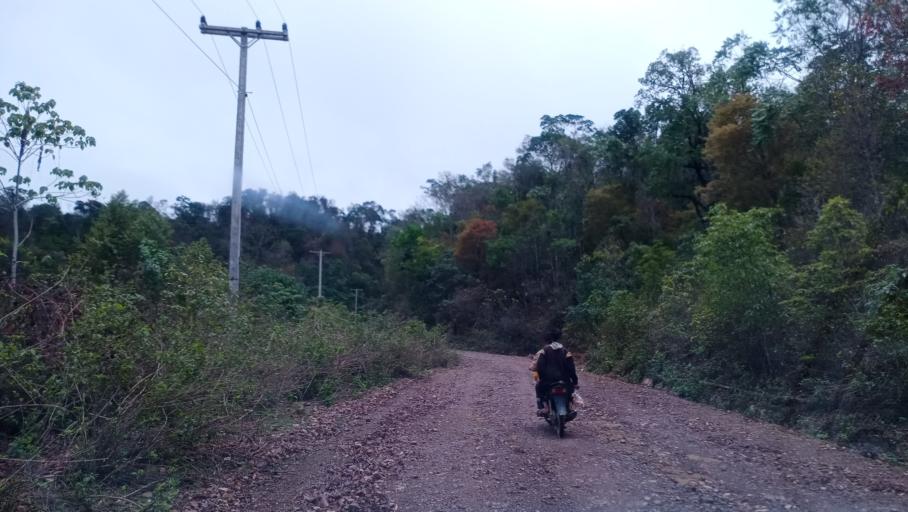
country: LA
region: Phongsali
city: Phongsali
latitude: 21.3465
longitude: 102.0953
